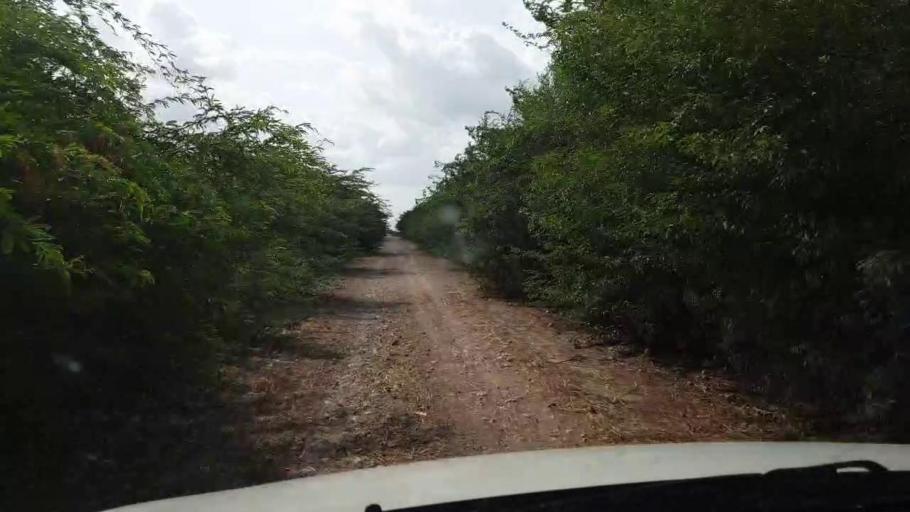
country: PK
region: Sindh
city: Kario
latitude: 24.6995
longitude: 68.6455
